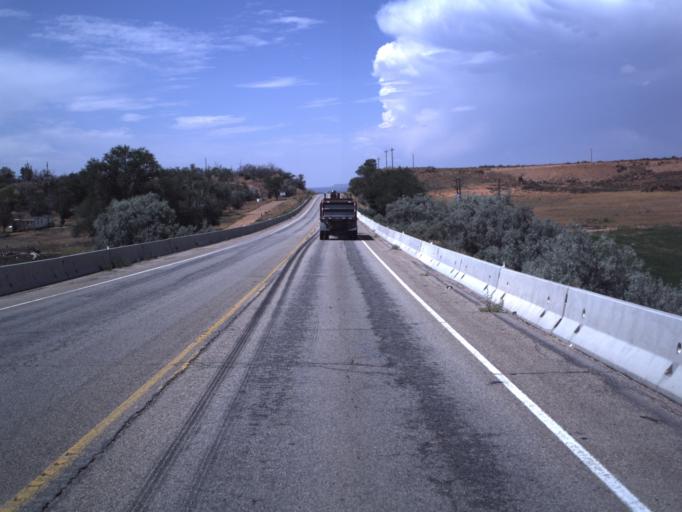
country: US
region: Utah
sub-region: Duchesne County
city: Roosevelt
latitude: 40.3020
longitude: -109.9096
